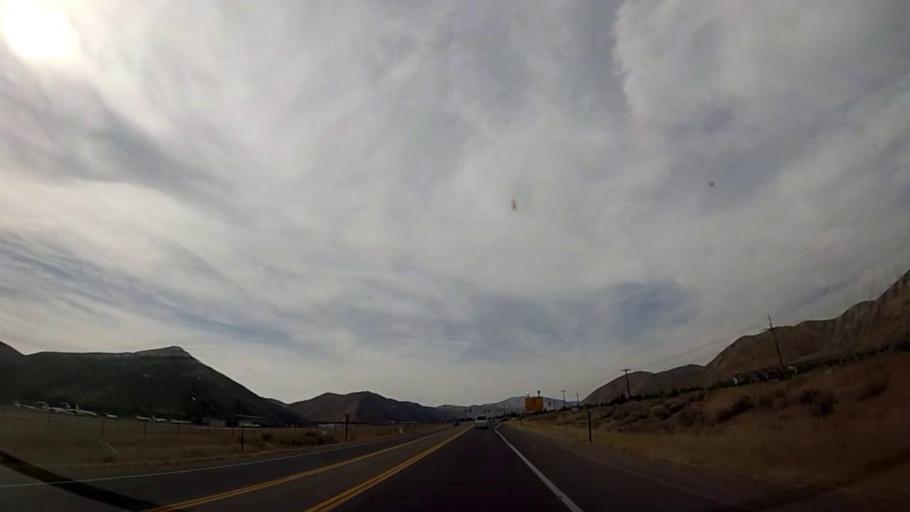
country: US
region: Idaho
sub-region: Blaine County
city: Hailey
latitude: 43.4970
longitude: -114.2872
